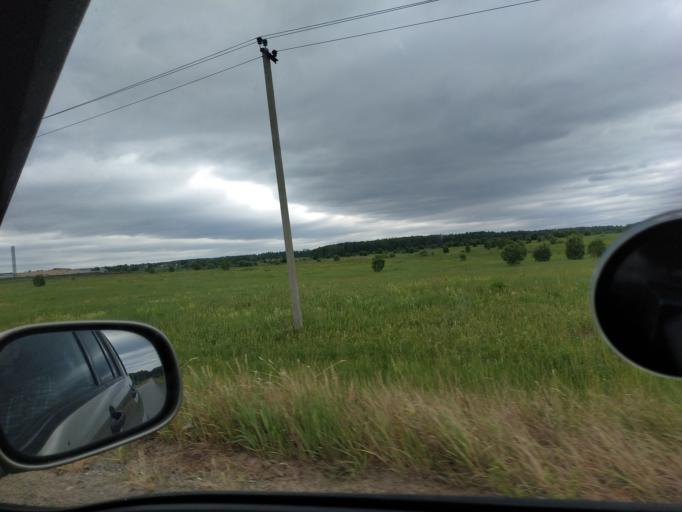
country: RU
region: Moskovskaya
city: Krasnoarmeysk
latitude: 56.0830
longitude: 38.2372
